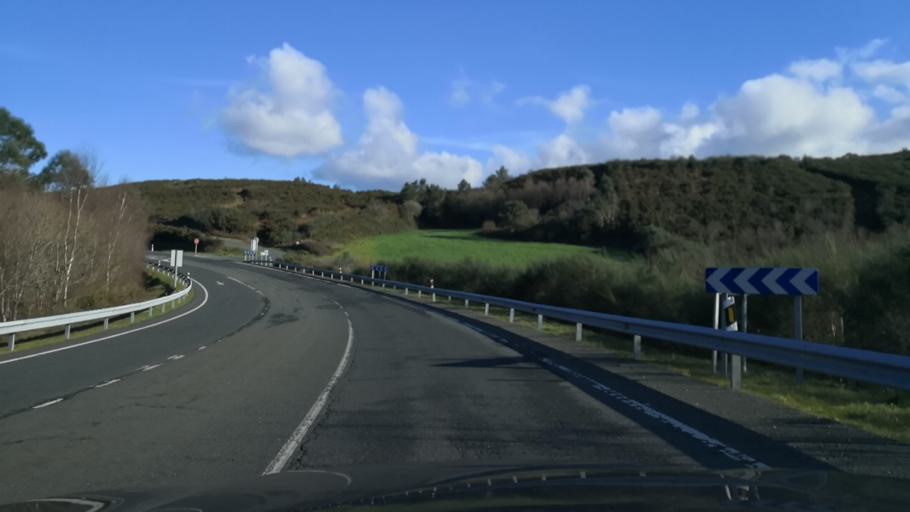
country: ES
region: Galicia
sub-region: Provincia de Pontevedra
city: Silleda
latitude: 42.6984
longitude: -8.3377
